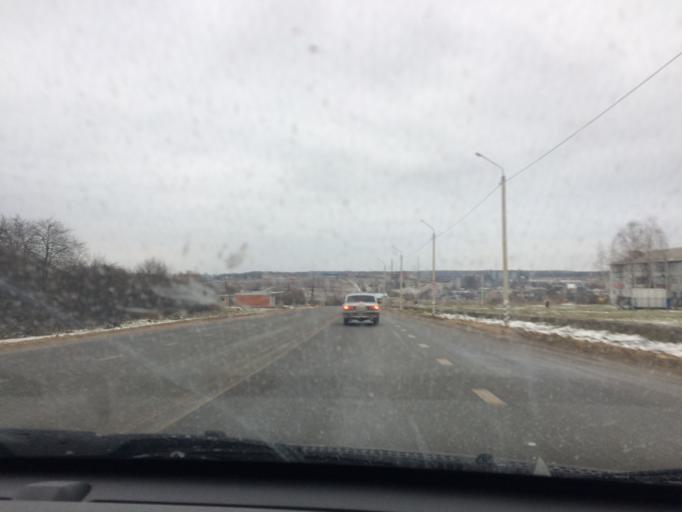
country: RU
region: Tula
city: Gorelki
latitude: 54.2537
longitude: 37.6951
